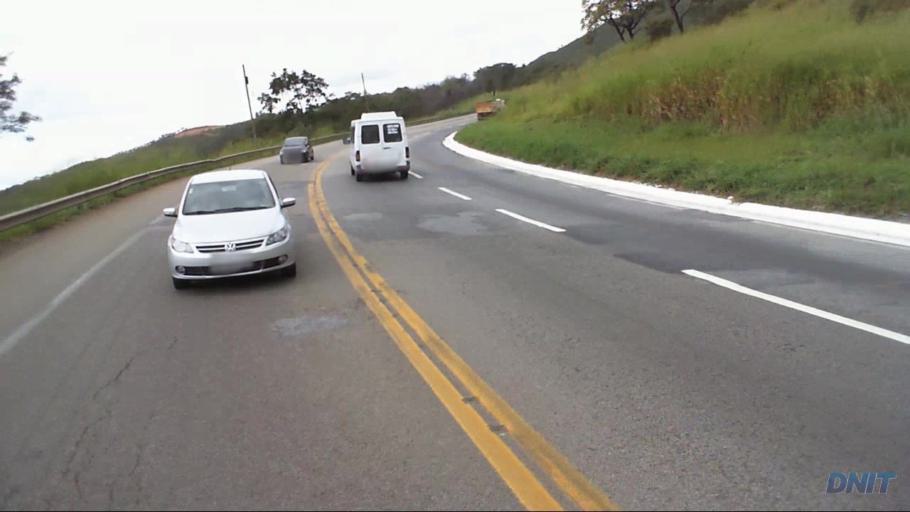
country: BR
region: Minas Gerais
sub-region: Caete
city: Caete
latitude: -19.7858
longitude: -43.7124
